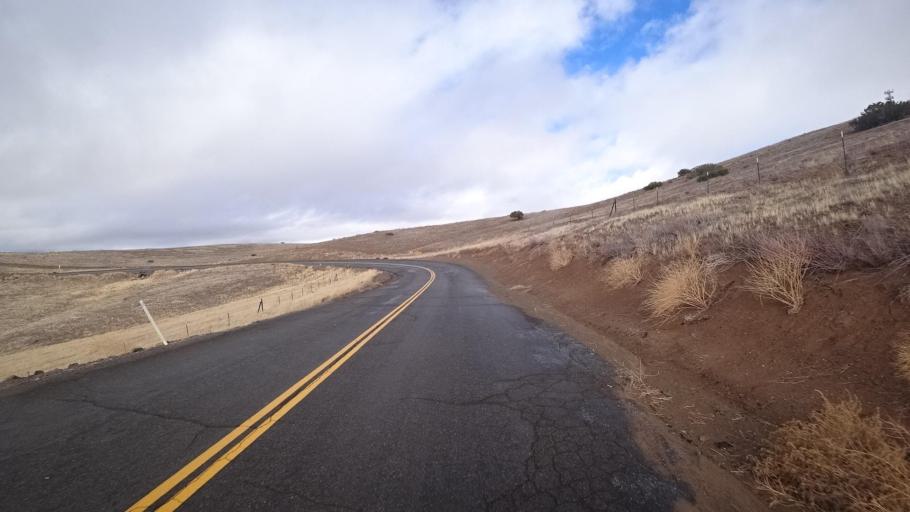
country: US
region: California
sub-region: Kern County
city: Maricopa
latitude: 34.9171
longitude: -119.4079
